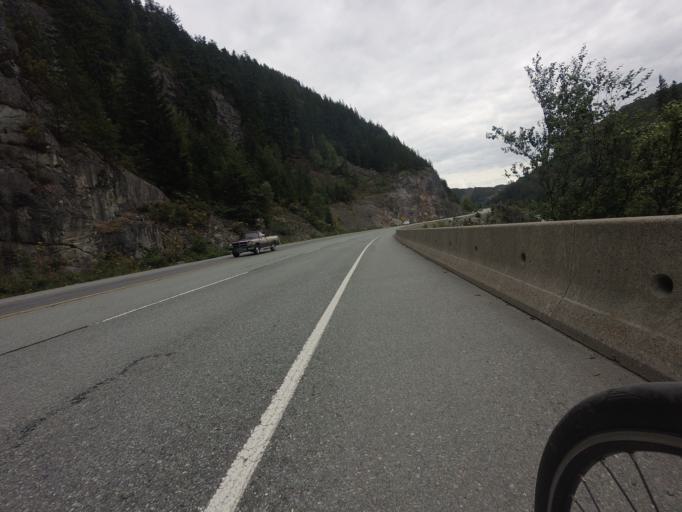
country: CA
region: British Columbia
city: Whistler
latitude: 49.9391
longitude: -123.1670
